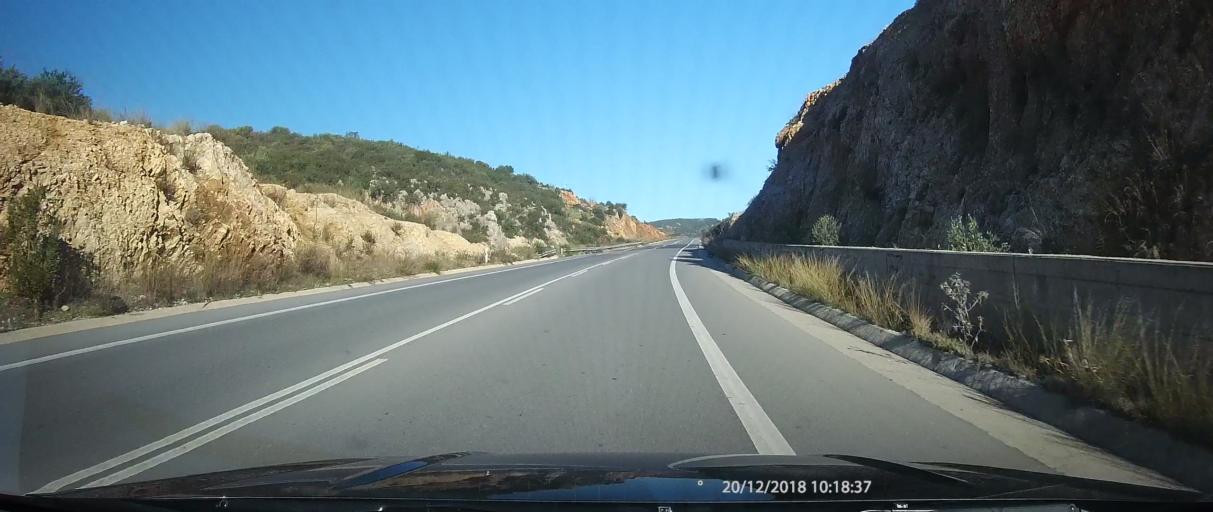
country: GR
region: Peloponnese
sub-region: Nomos Lakonias
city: Magoula
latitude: 37.1194
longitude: 22.4213
